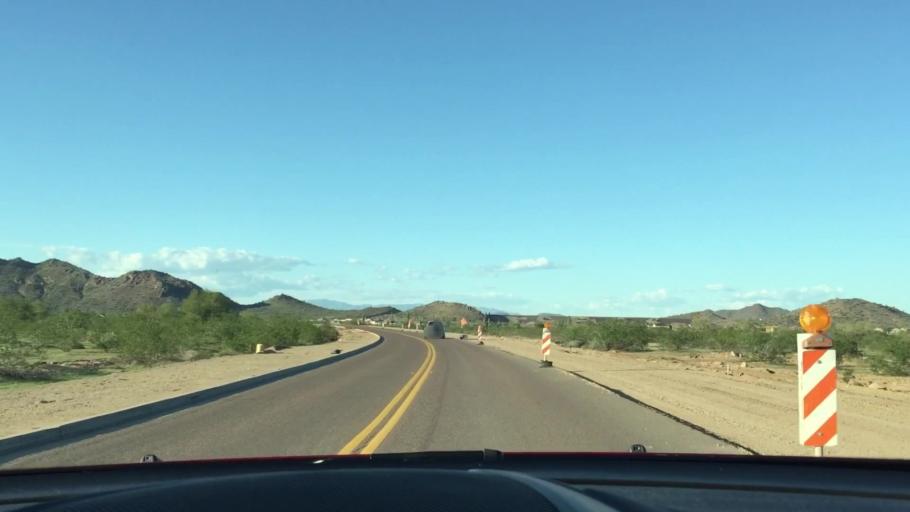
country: US
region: Arizona
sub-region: Maricopa County
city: Sun City West
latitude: 33.7159
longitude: -112.2326
